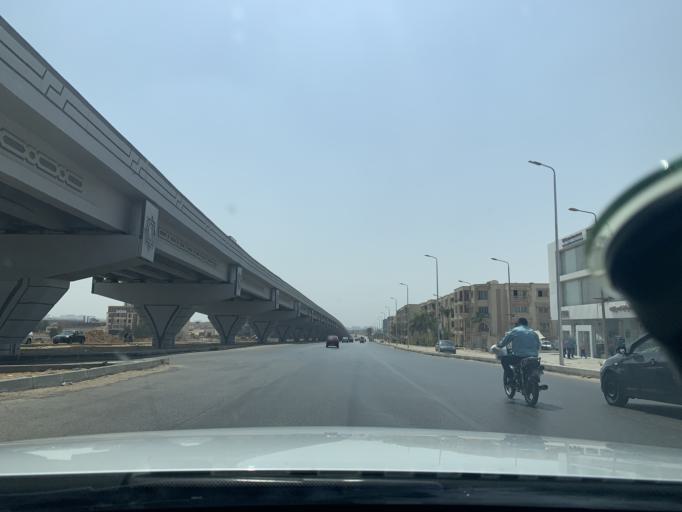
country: EG
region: Muhafazat al Qalyubiyah
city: Al Khankah
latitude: 30.0916
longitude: 31.3788
